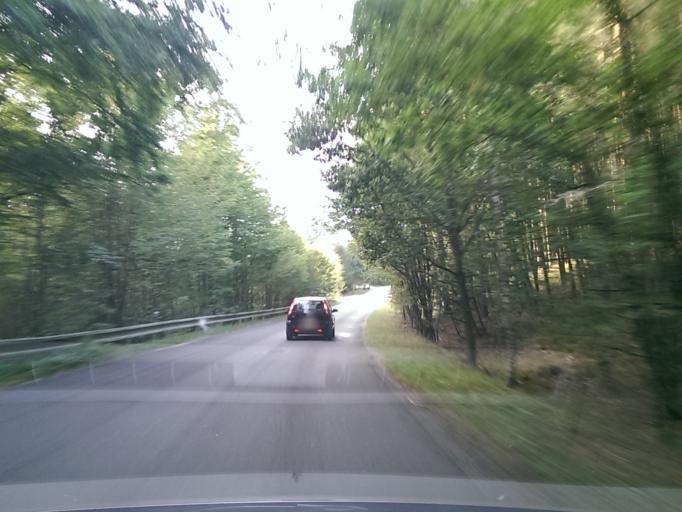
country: CZ
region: Central Bohemia
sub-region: Okres Mlada Boleslav
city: Zd'ar
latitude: 50.5002
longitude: 15.1197
